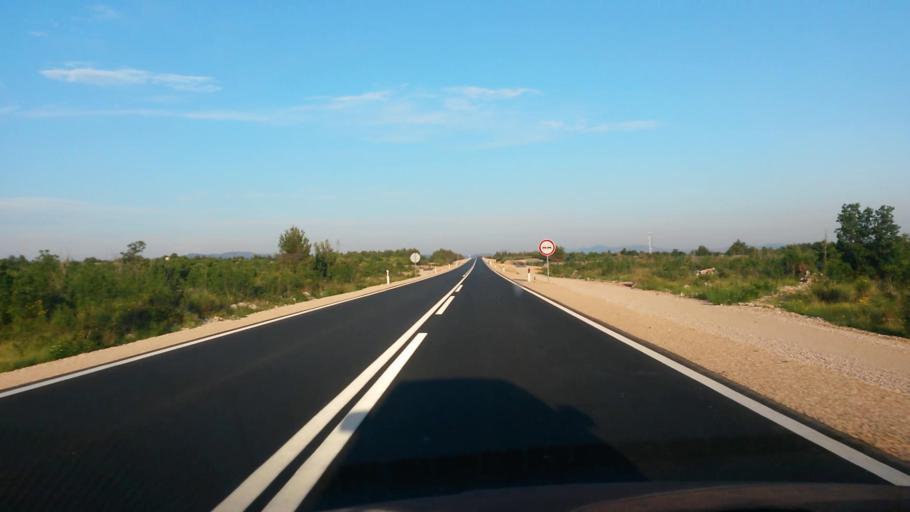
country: HR
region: Sibensko-Kniniska
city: Vodice
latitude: 43.7708
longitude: 15.7932
